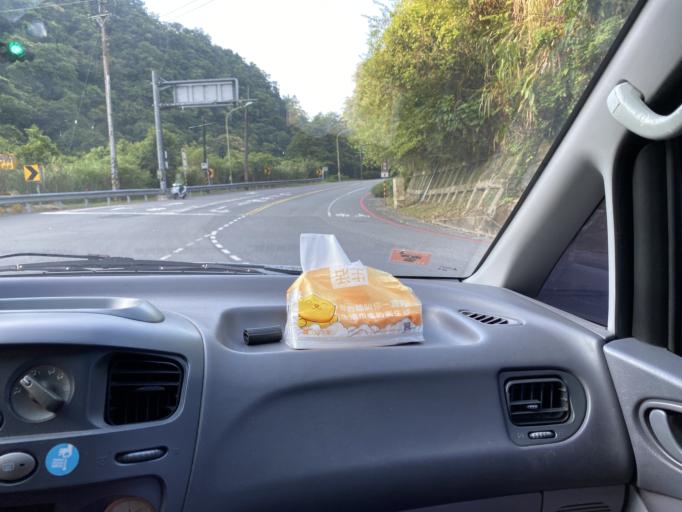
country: TW
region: Taiwan
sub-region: Keelung
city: Keelung
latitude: 25.0388
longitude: 121.7801
